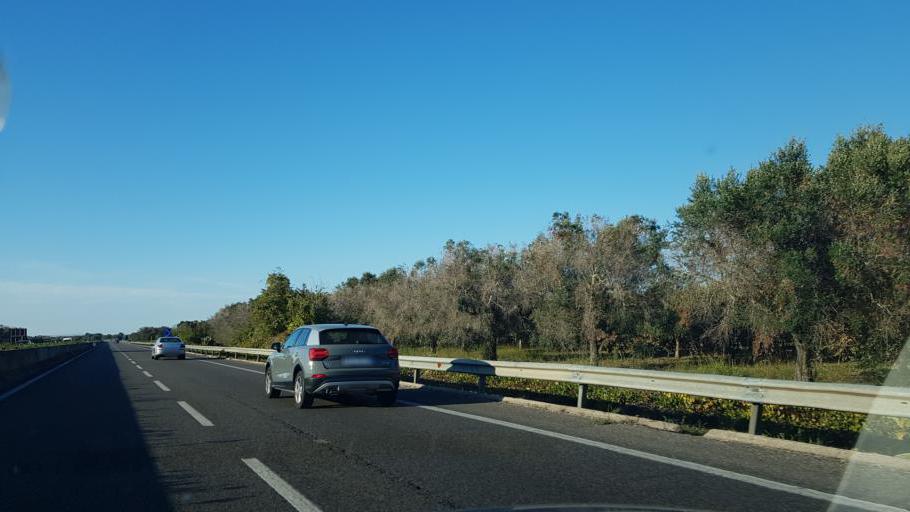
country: IT
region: Apulia
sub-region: Provincia di Brindisi
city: San Pietro Vernotico
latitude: 40.5261
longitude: 18.0134
